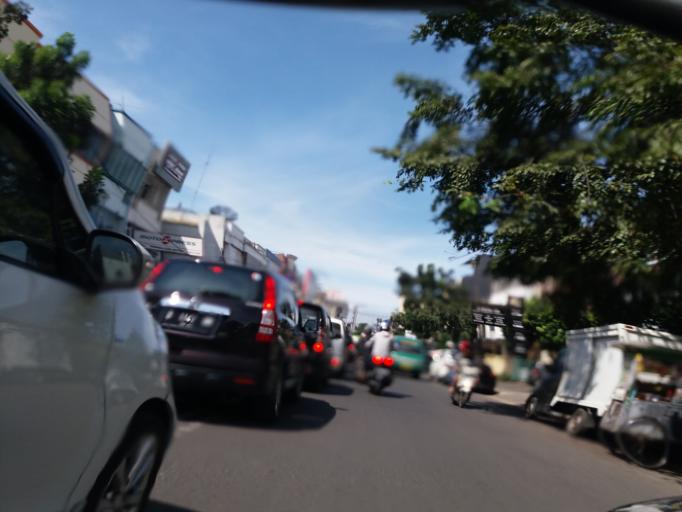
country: ID
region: West Java
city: Bandung
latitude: -6.9266
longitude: 107.5969
